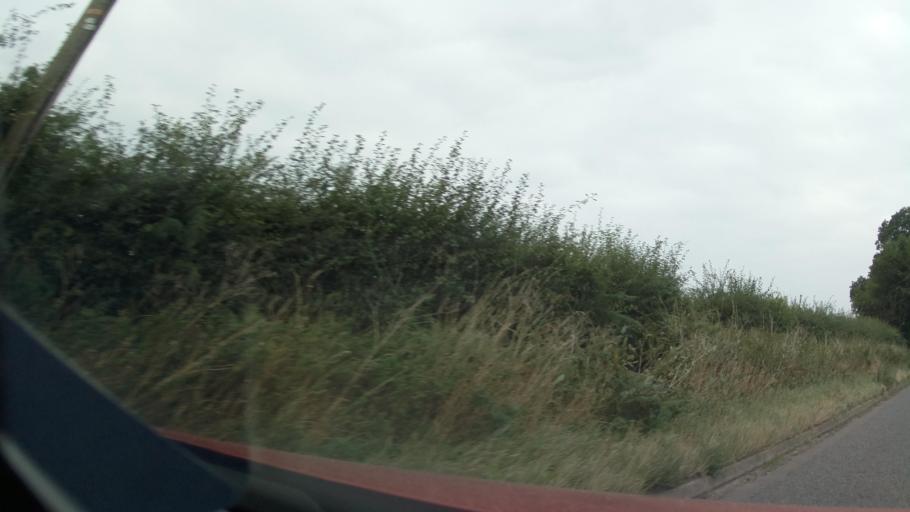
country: GB
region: England
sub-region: Shropshire
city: Shawbury
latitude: 52.8212
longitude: -2.6073
